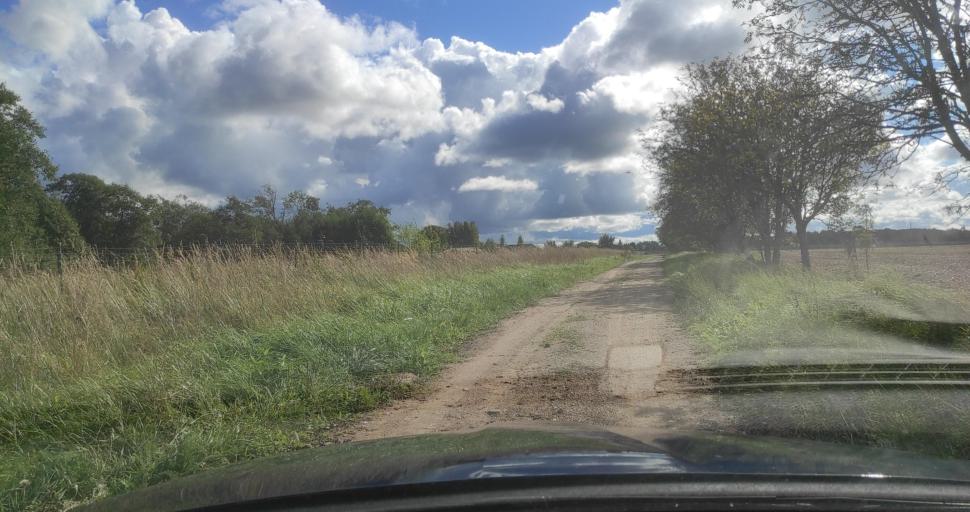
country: LV
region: Ventspils Rajons
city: Piltene
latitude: 57.2687
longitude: 21.6043
